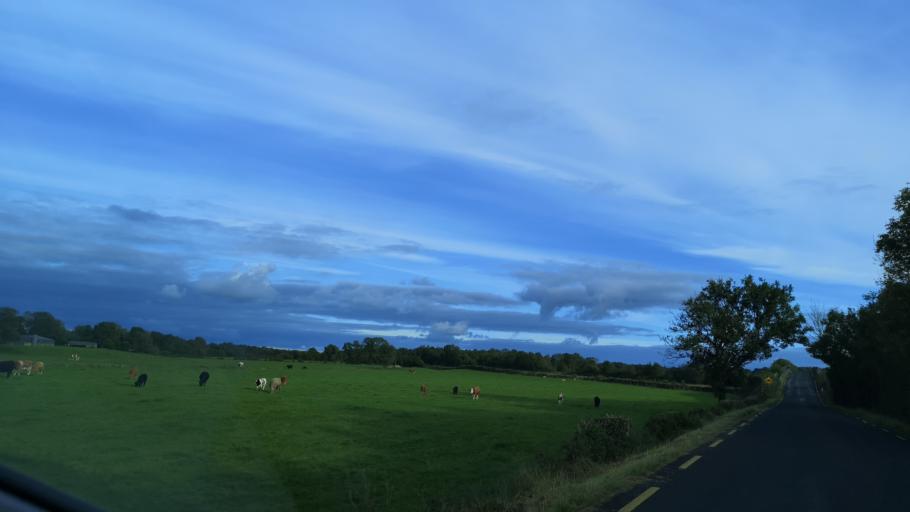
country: IE
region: Connaught
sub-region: County Galway
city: Ballinasloe
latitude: 53.3337
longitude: -8.2834
